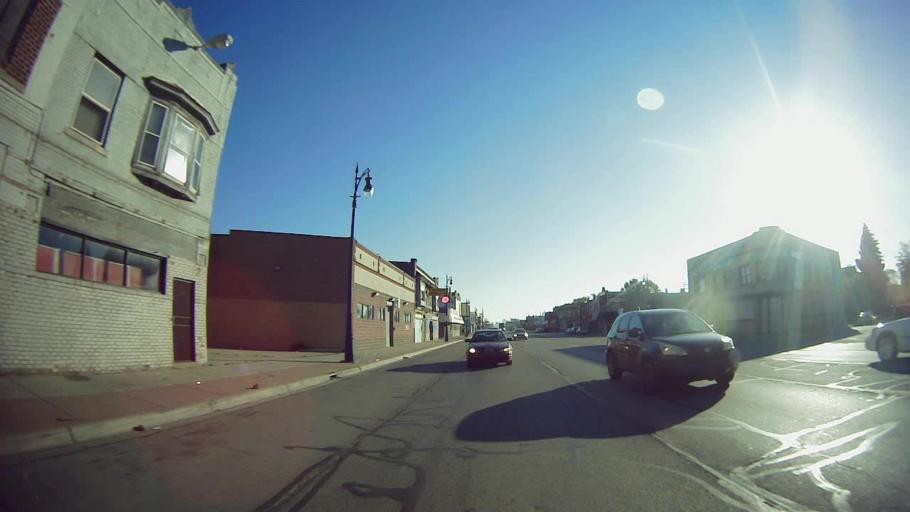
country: US
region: Michigan
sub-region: Wayne County
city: Dearborn
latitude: 42.3312
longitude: -83.1342
